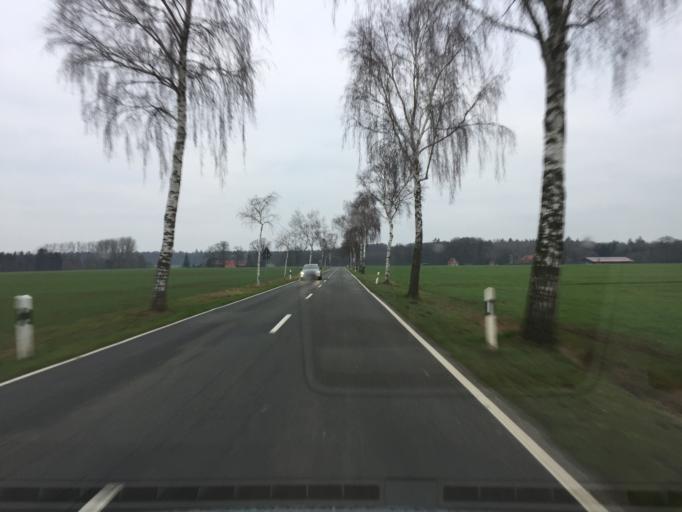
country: DE
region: Lower Saxony
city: Sudwalde
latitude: 52.8072
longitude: 8.8423
